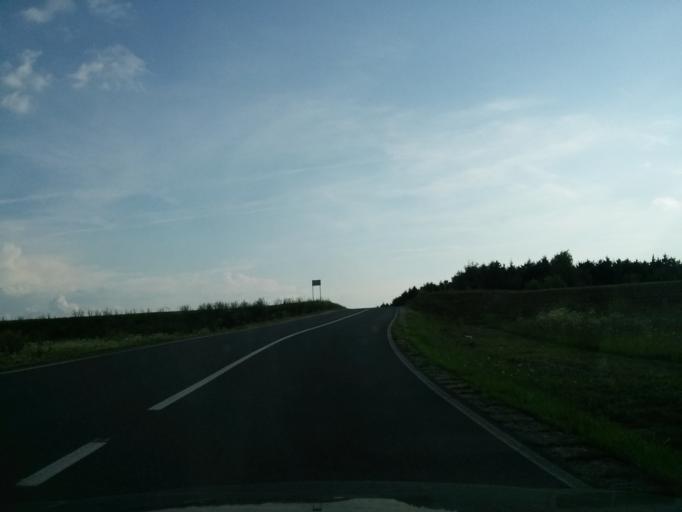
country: HR
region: Grad Zagreb
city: Zadvorsko
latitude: 45.7469
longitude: 15.9205
